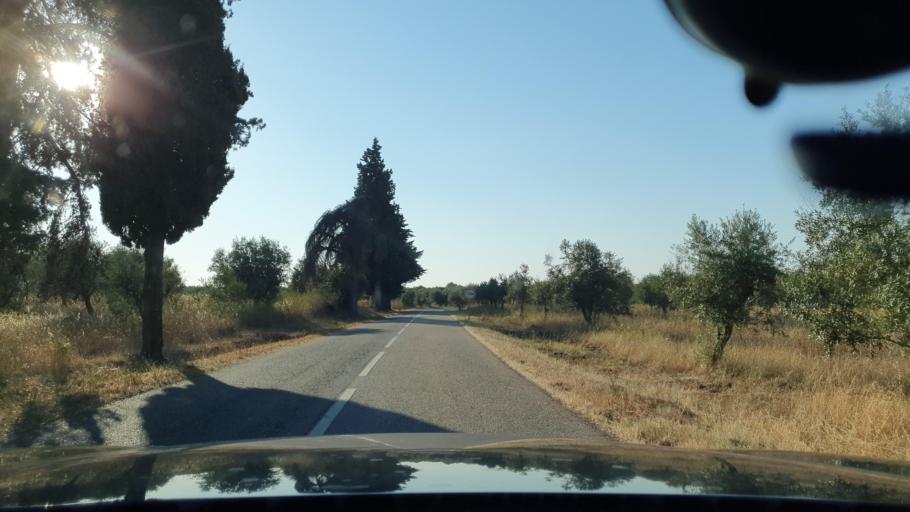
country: PT
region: Portalegre
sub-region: Fronteira
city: Fronteira
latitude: 38.9386
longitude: -7.6739
